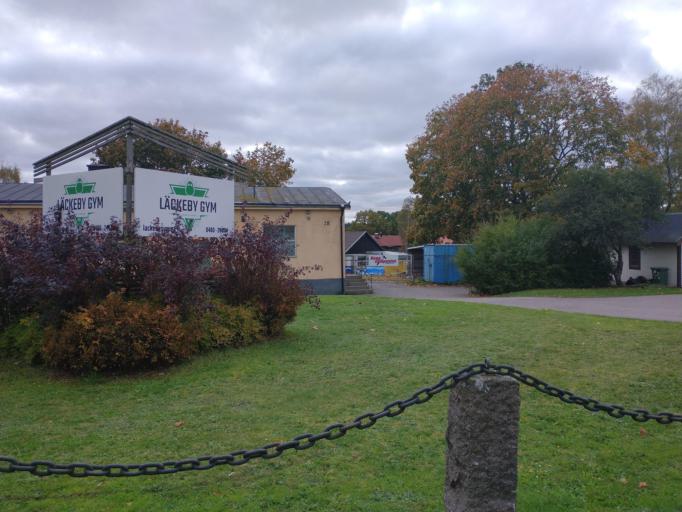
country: SE
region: Kalmar
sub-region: Kalmar Kommun
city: Lindsdal
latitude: 56.7828
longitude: 16.2967
